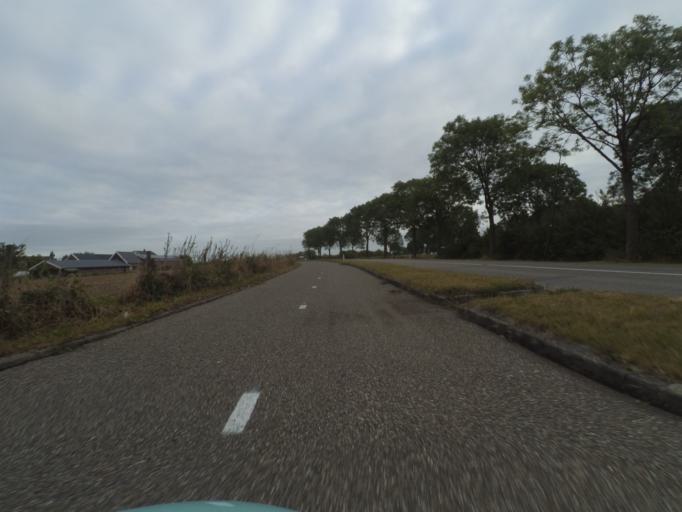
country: NL
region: Utrecht
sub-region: Gemeente Wijk bij Duurstede
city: Wijk bij Duurstede
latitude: 51.9749
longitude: 5.3210
